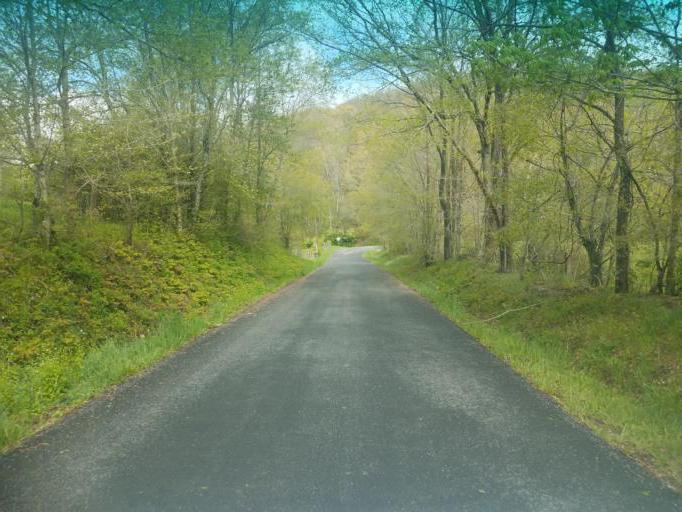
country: US
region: Virginia
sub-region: Smyth County
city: Atkins
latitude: 36.9451
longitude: -81.4161
